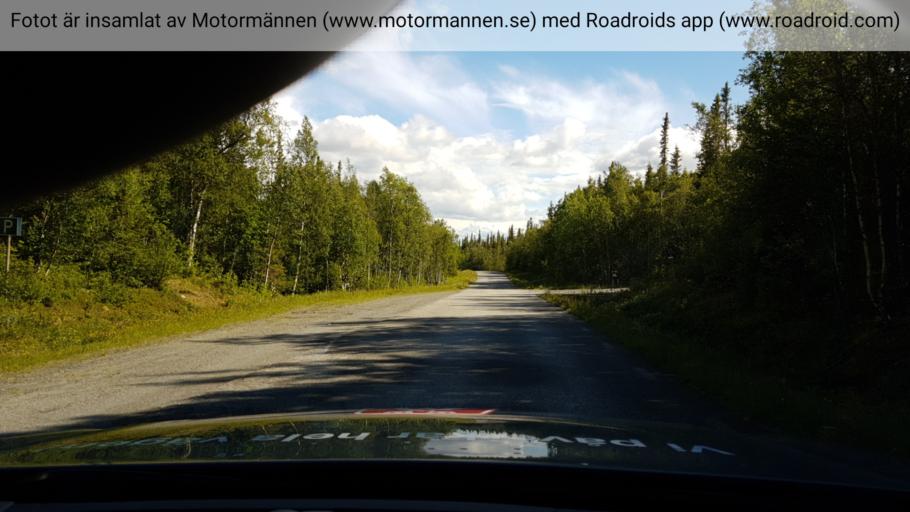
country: SE
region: Jaemtland
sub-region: Bergs Kommun
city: Hoverberg
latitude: 63.0105
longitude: 13.9423
